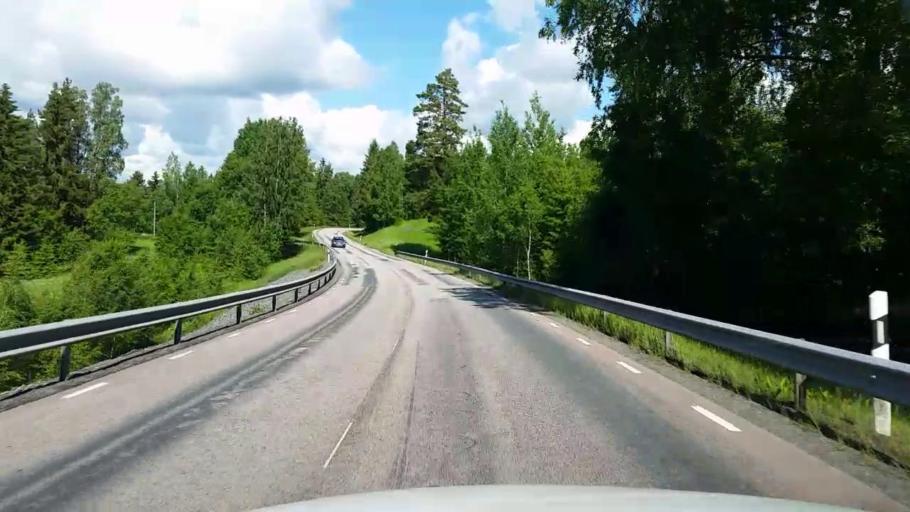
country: SE
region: Vaestmanland
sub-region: Kopings Kommun
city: Kolsva
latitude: 59.6325
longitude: 15.8023
